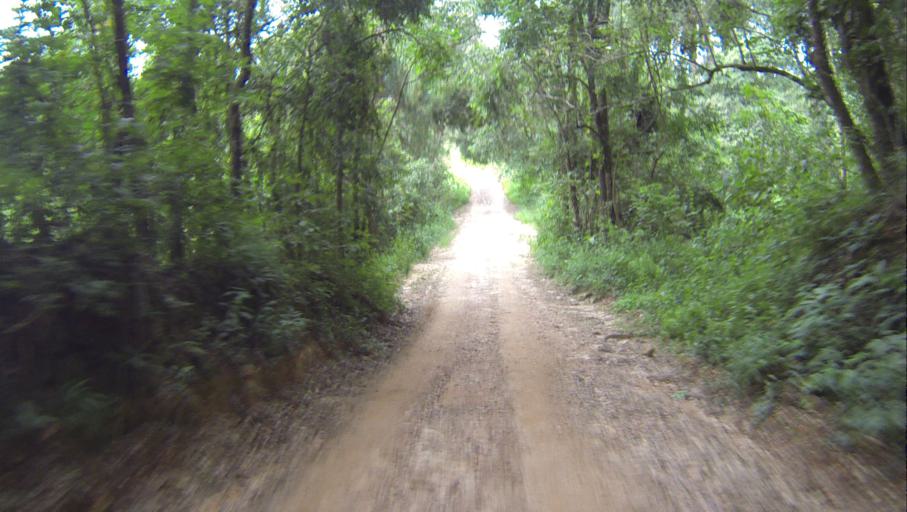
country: BR
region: Minas Gerais
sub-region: Brumadinho
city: Brumadinho
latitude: -20.1596
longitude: -44.1297
